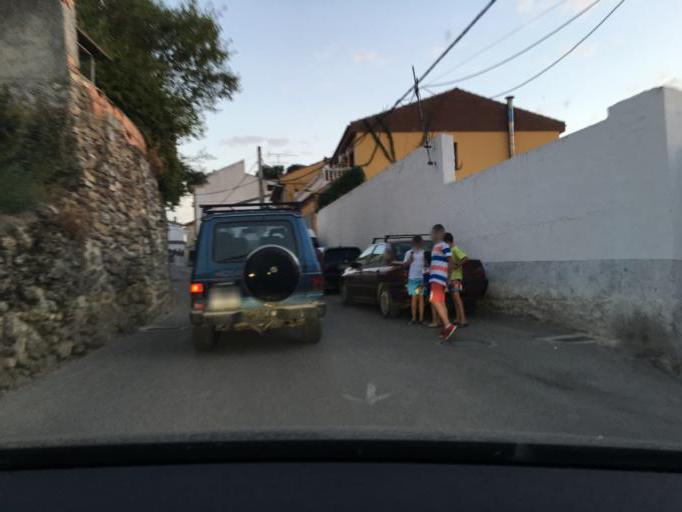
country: ES
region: Andalusia
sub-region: Provincia de Granada
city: Beas de Granada
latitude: 37.2194
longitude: -3.4817
